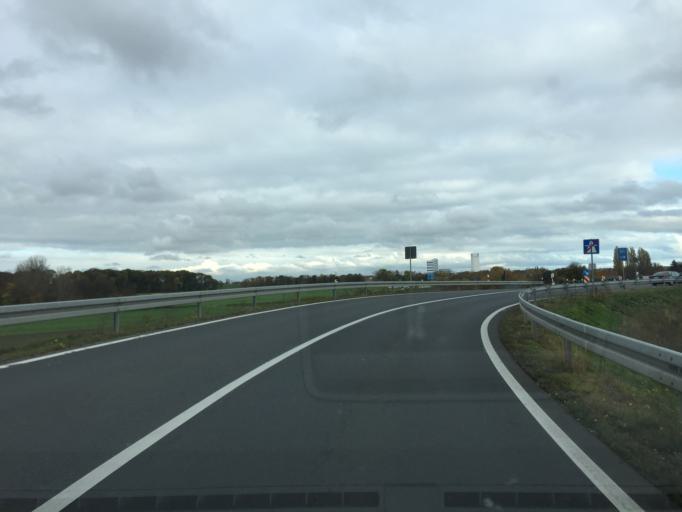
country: DE
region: Lower Saxony
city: Leiferde
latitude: 52.2107
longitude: 10.4886
